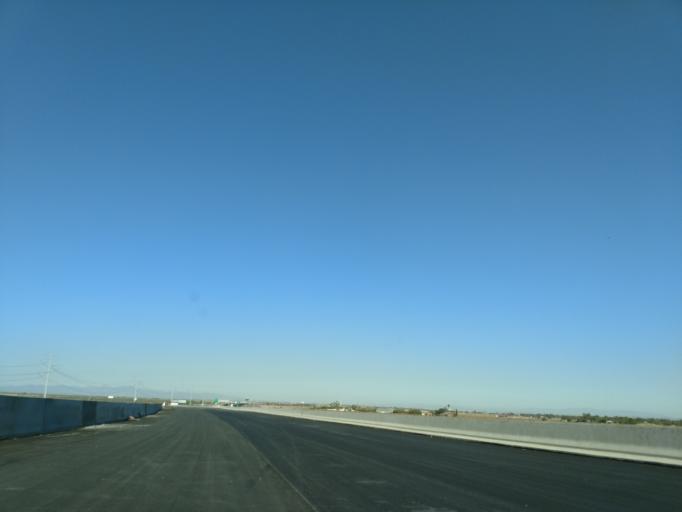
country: US
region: Arizona
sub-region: Maricopa County
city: Laveen
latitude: 33.3256
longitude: -112.1671
